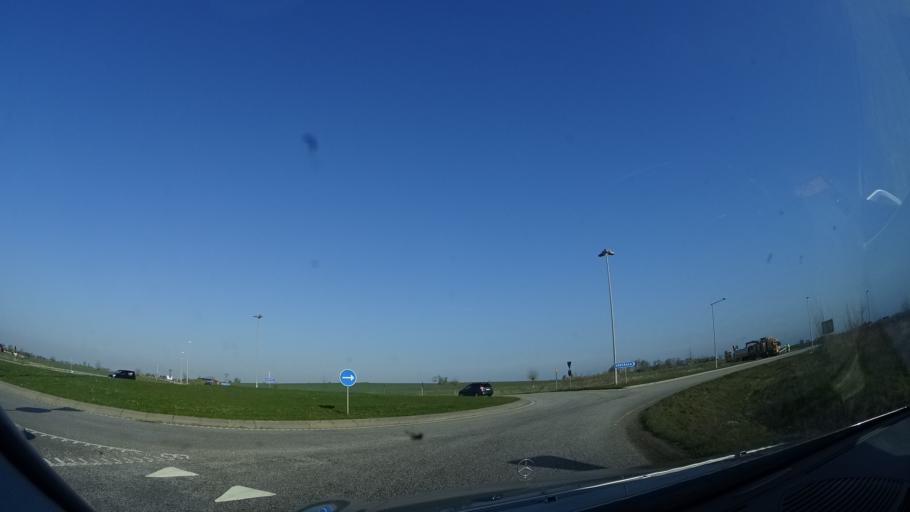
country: SE
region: Skane
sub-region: Svalovs Kommun
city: Svaloev
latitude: 55.8759
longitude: 13.1622
